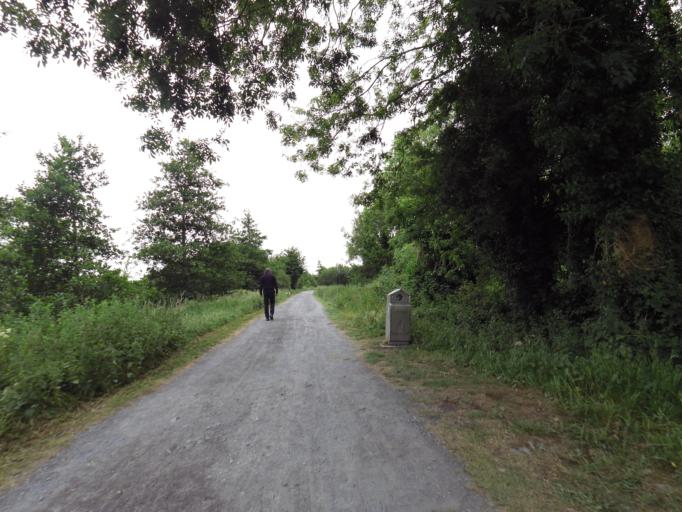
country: IE
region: Connaught
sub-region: County Galway
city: Gaillimh
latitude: 53.2910
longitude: -9.0669
